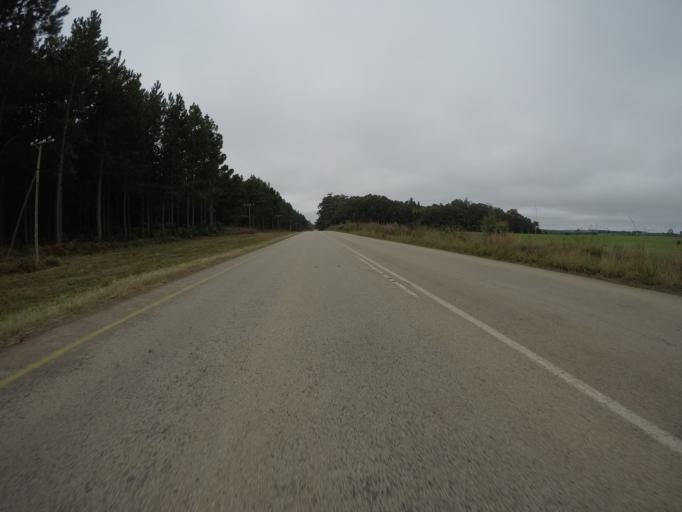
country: ZA
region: Eastern Cape
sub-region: Cacadu District Municipality
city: Kareedouw
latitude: -33.9941
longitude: 24.1067
